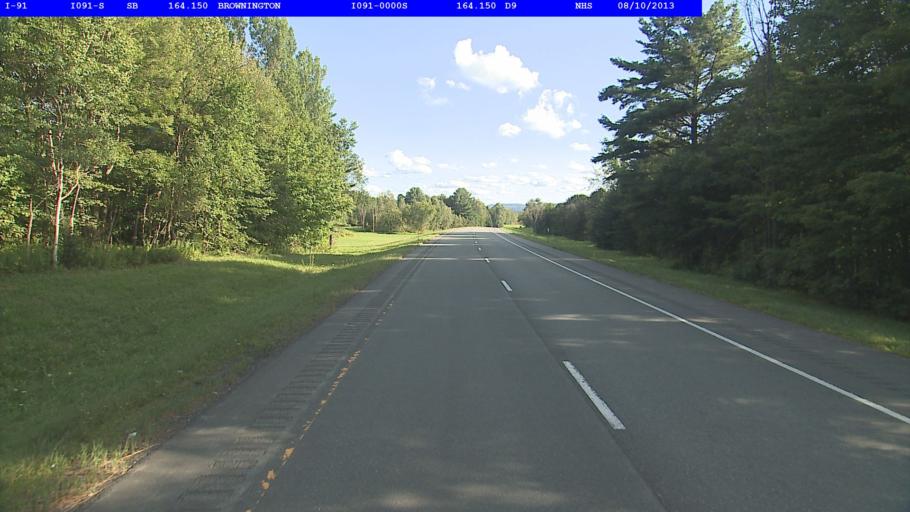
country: US
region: Vermont
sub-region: Orleans County
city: Newport
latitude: 44.8428
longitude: -72.1935
